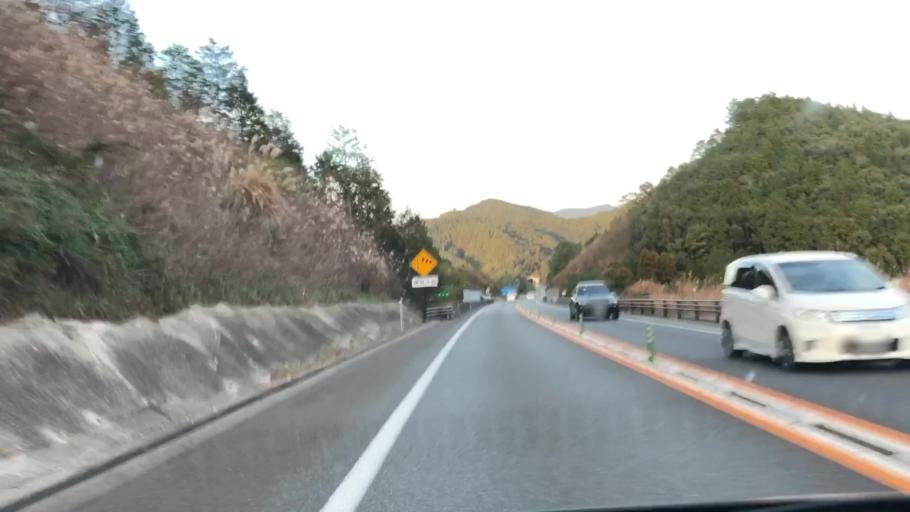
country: JP
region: Kumamoto
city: Minamata
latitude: 32.2759
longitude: 130.4952
